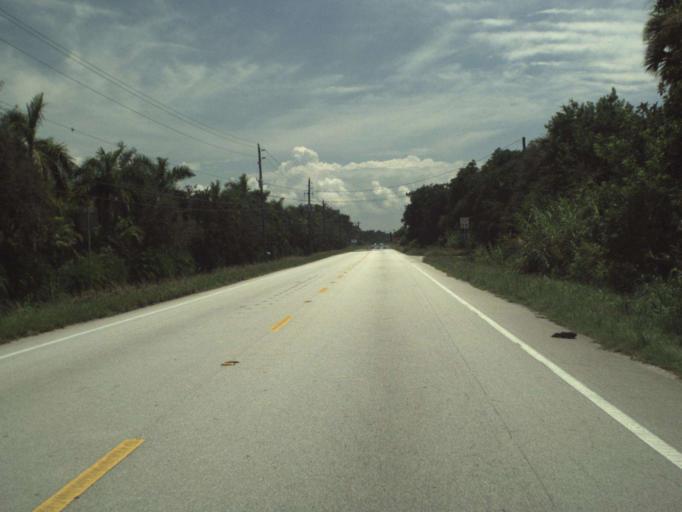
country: US
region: Florida
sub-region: Martin County
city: Indiantown
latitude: 26.9564
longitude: -80.6097
